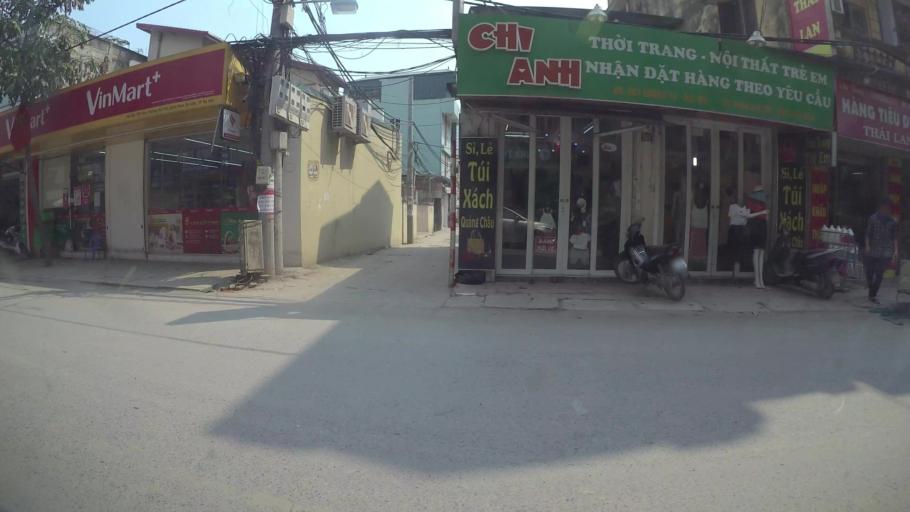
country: VN
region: Ha Noi
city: Ha Dong
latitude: 20.9952
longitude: 105.7580
